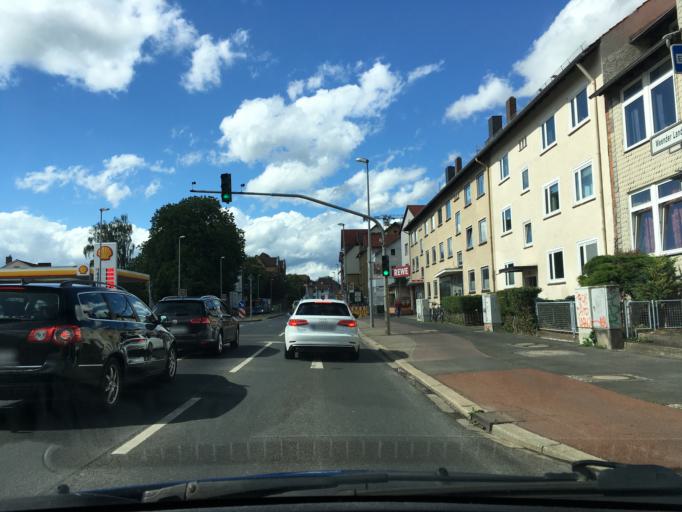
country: DE
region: Lower Saxony
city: Goettingen
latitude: 51.5449
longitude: 9.9319
